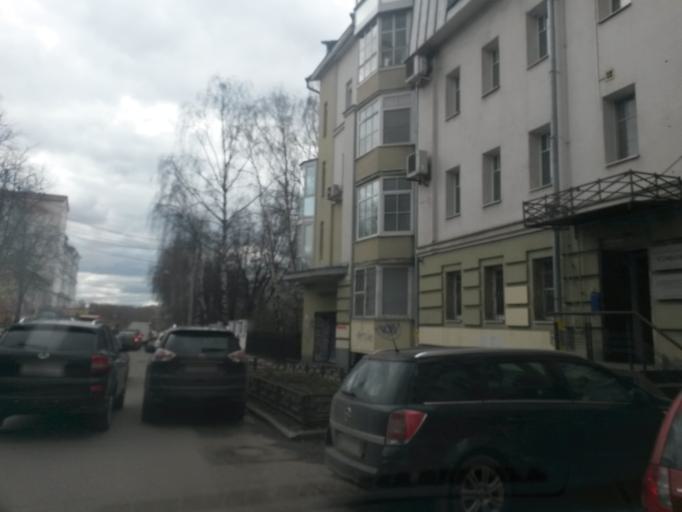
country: RU
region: Jaroslavl
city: Yaroslavl
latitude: 57.6215
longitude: 39.8772
